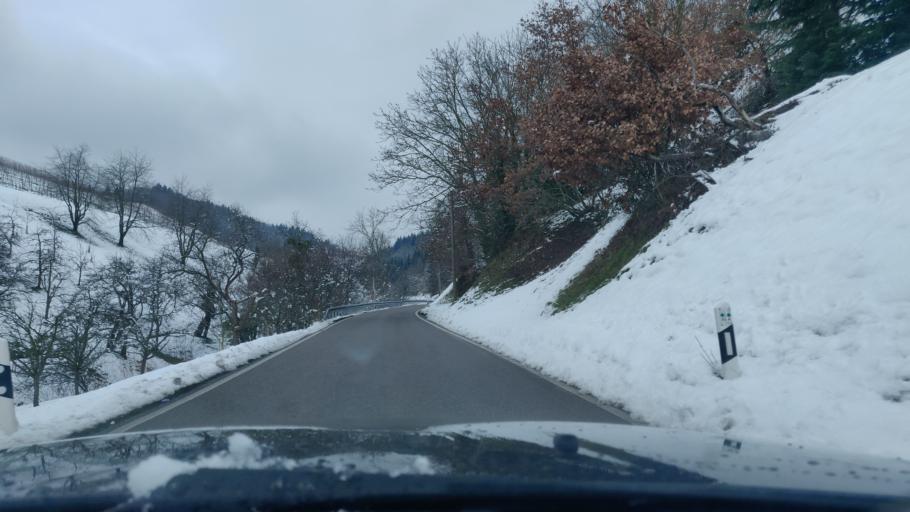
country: DE
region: Baden-Wuerttemberg
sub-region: Freiburg Region
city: Oberkirch
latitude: 48.5587
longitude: 8.0896
